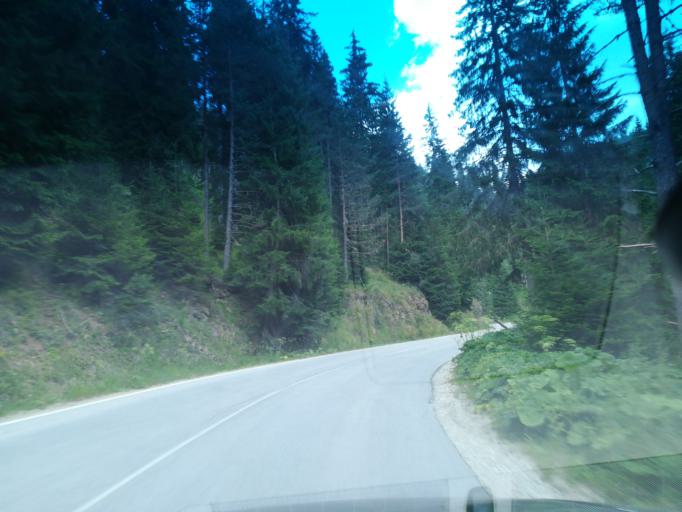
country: BG
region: Smolyan
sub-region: Obshtina Chepelare
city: Chepelare
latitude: 41.6627
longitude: 24.6574
